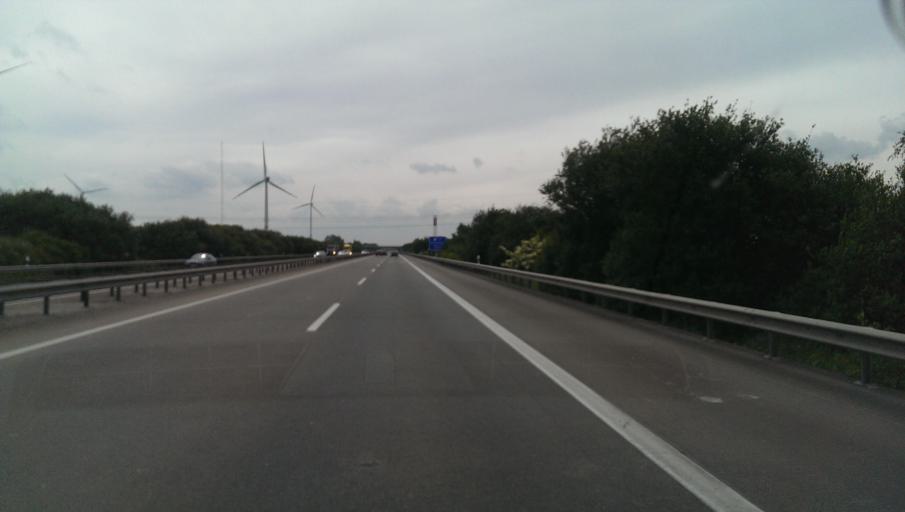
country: DE
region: Lower Saxony
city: Schiffdorf
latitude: 53.5615
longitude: 8.6195
